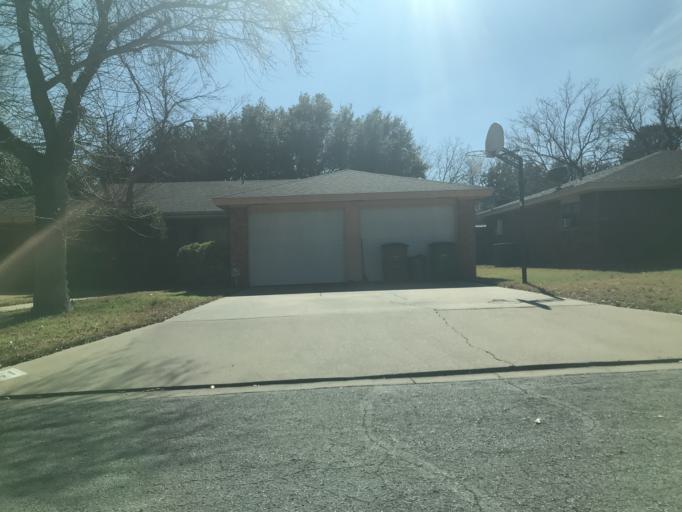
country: US
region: Texas
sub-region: Tom Green County
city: San Angelo
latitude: 31.4291
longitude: -100.4924
